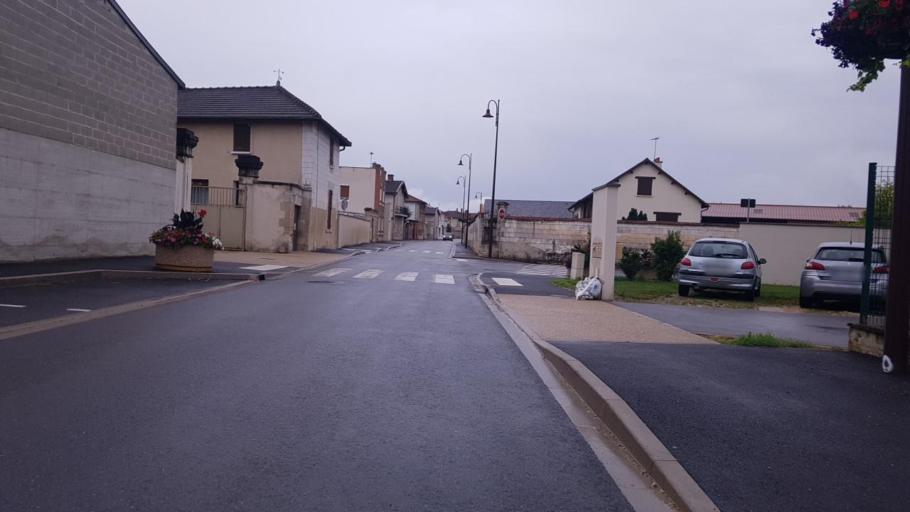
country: FR
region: Champagne-Ardenne
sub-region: Departement de la Marne
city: Sarry
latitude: 48.9175
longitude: 4.4086
